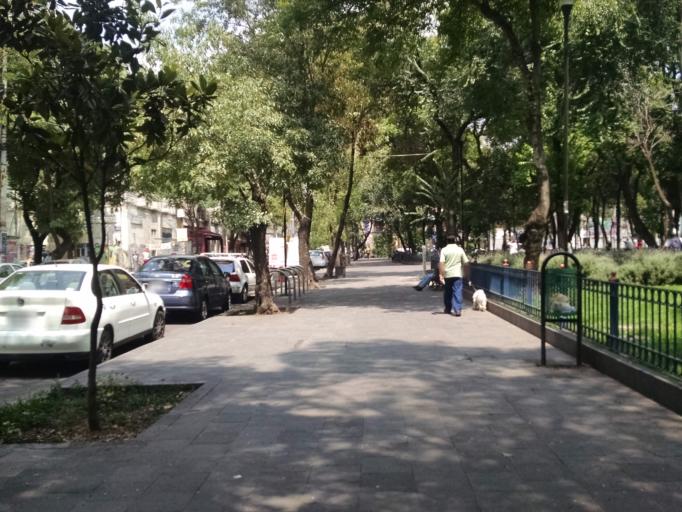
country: MX
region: Mexico City
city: Cuauhtemoc
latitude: 19.4488
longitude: -99.1567
